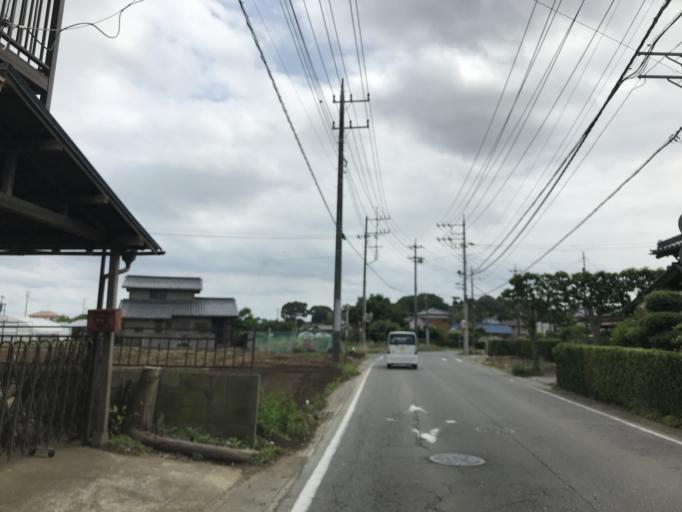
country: JP
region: Ibaraki
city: Ushiku
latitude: 35.9780
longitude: 140.0975
